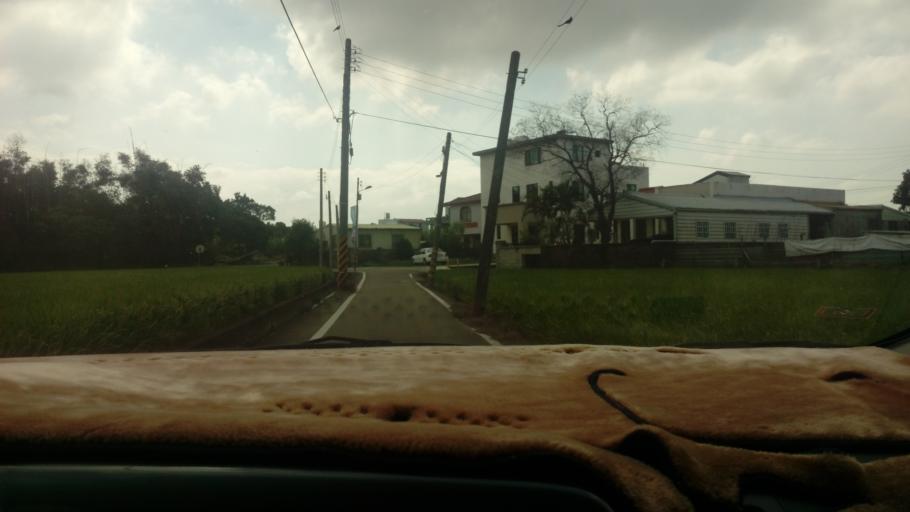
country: TW
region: Taiwan
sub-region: Miaoli
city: Miaoli
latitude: 24.5668
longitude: 120.8373
